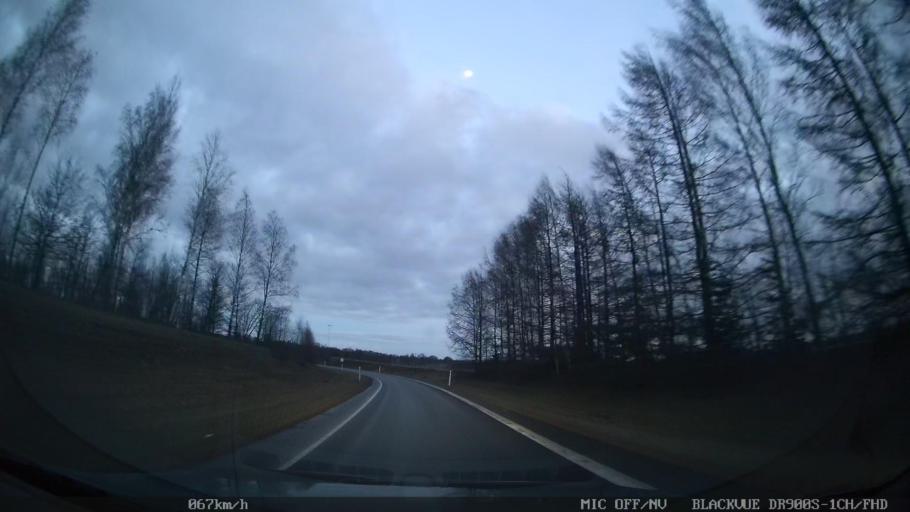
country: SE
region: Skane
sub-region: Hassleholms Kommun
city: Hassleholm
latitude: 56.1794
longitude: 13.7526
